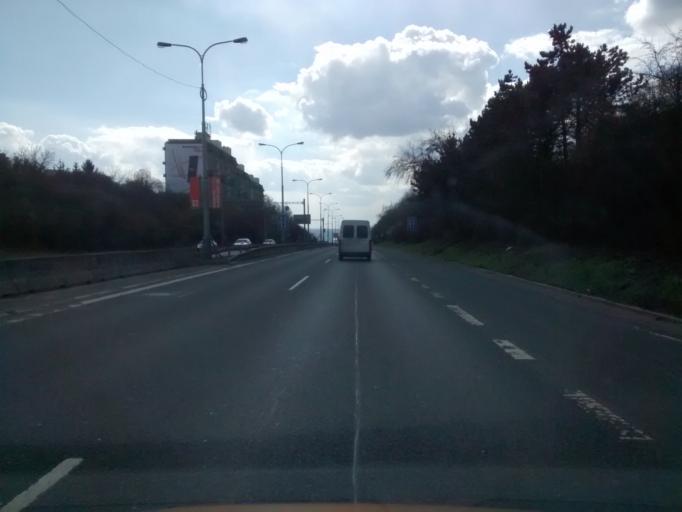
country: CZ
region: Praha
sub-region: Praha 9
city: Strizkov
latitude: 50.1281
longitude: 14.4851
